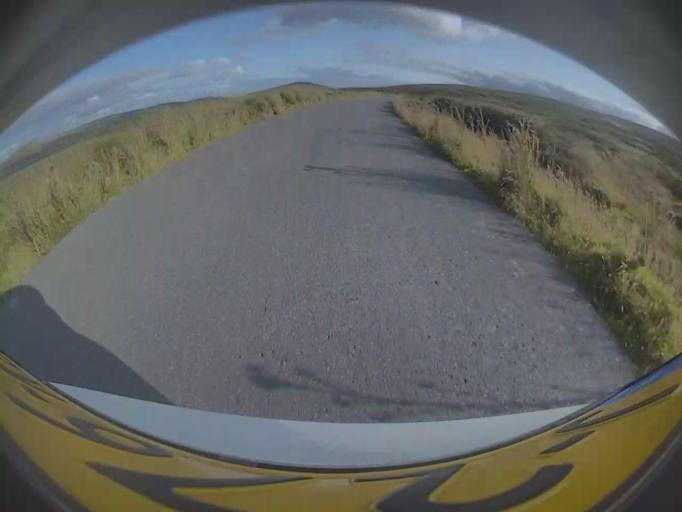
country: IE
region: Leinster
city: Ballyboden
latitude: 53.1342
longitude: -6.3092
